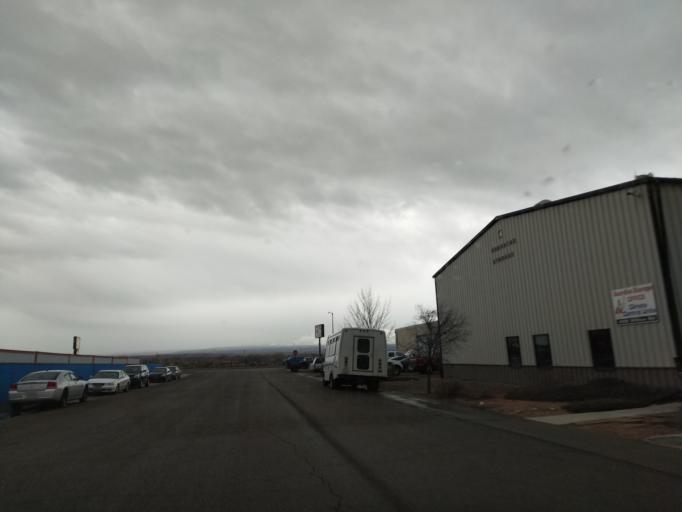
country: US
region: Colorado
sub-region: Mesa County
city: Grand Junction
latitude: 39.0717
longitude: -108.5263
